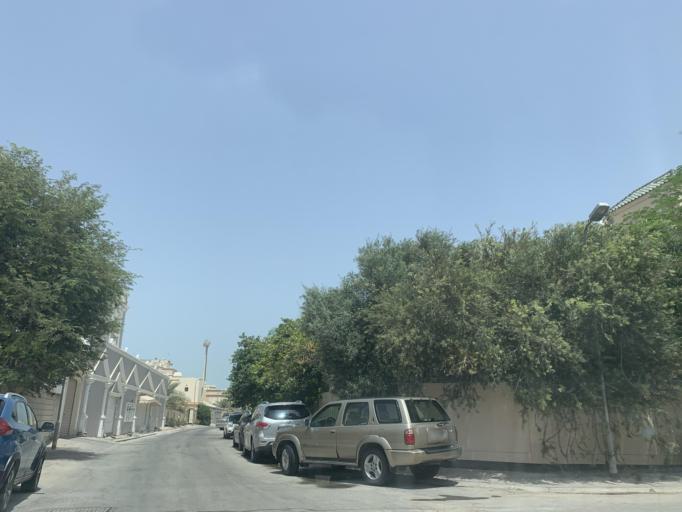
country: BH
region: Northern
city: Madinat `Isa
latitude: 26.1675
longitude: 50.5700
